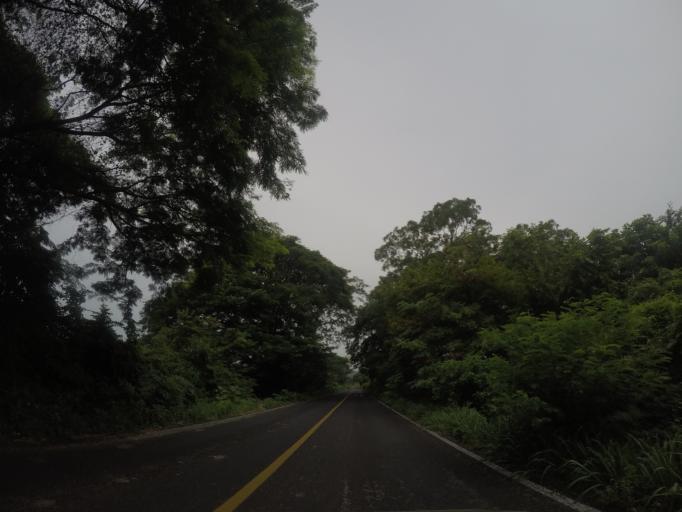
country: MX
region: Oaxaca
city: San Pedro Mixtepec
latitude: 15.9573
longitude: -97.2432
